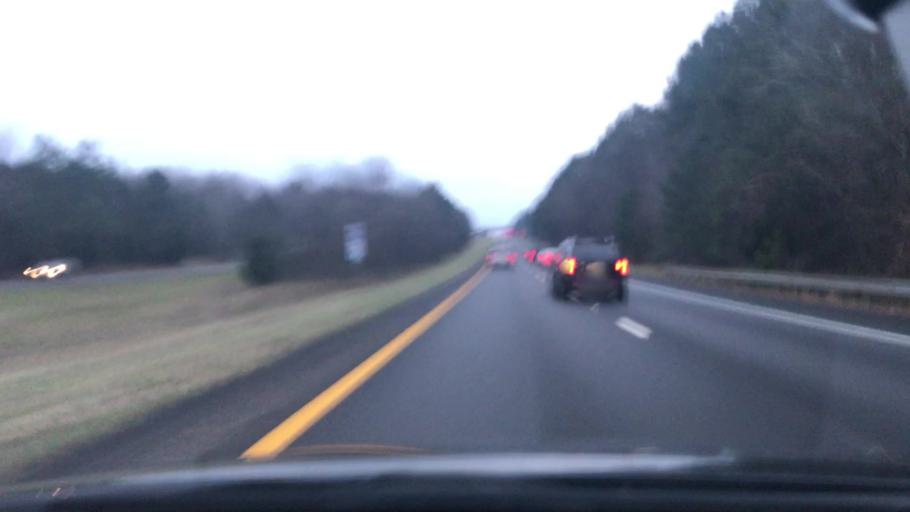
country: US
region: Tennessee
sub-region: Sumner County
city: White House
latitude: 36.4425
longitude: -86.7023
